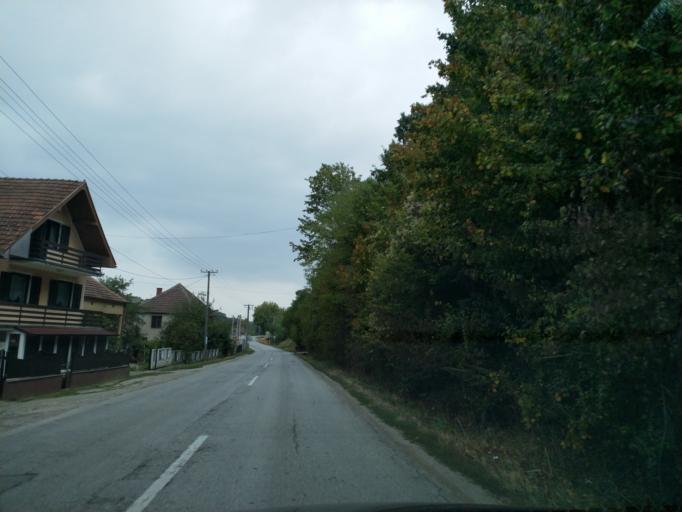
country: RS
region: Central Serbia
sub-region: Pomoravski Okrug
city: Jagodina
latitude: 44.0392
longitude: 21.1882
